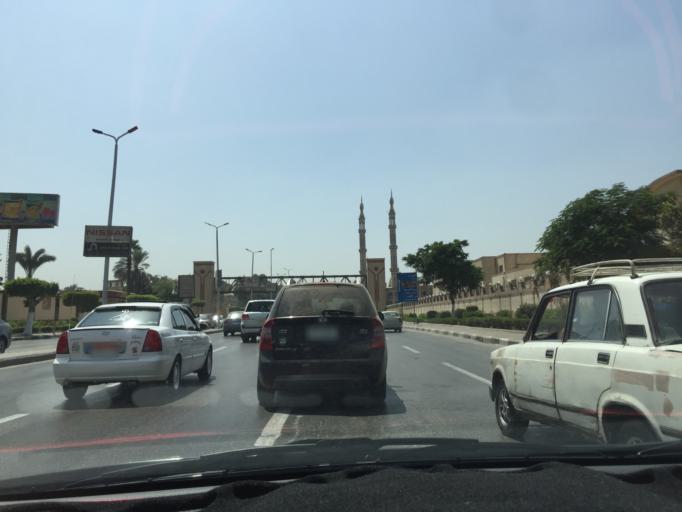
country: EG
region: Muhafazat al Qahirah
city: Cairo
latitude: 30.0640
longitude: 31.2863
